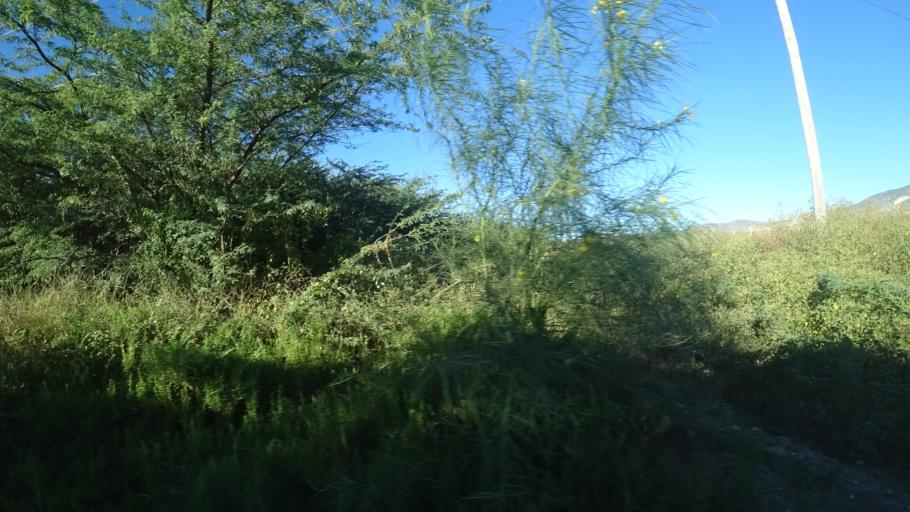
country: HT
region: Ouest
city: Croix des Bouquets
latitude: 18.6538
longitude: -72.2244
